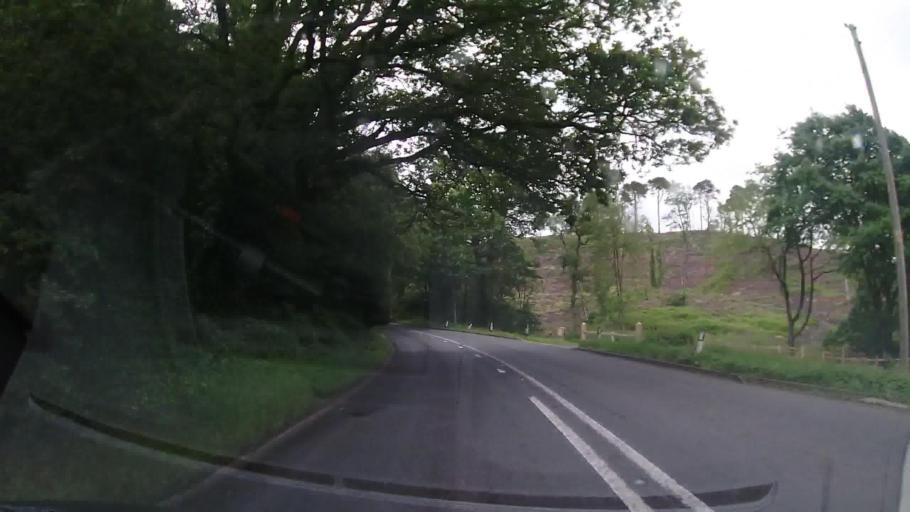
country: GB
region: England
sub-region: Staffordshire
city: Standon
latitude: 52.9506
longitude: -2.3266
